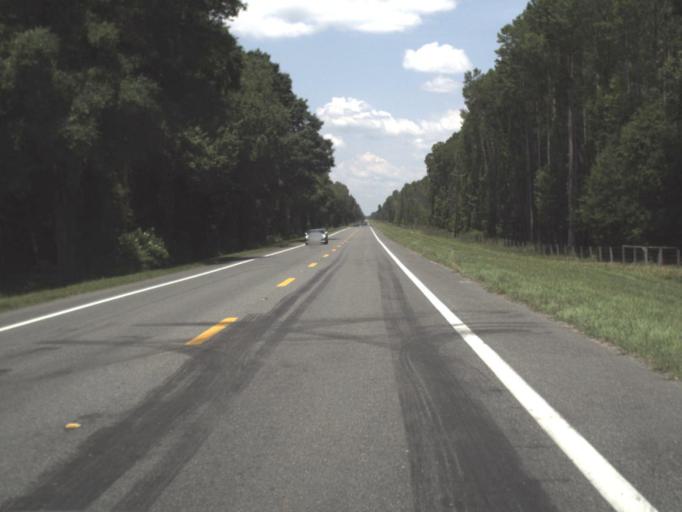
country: US
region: Florida
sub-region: Union County
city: Lake Butler
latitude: 30.0382
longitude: -82.3791
